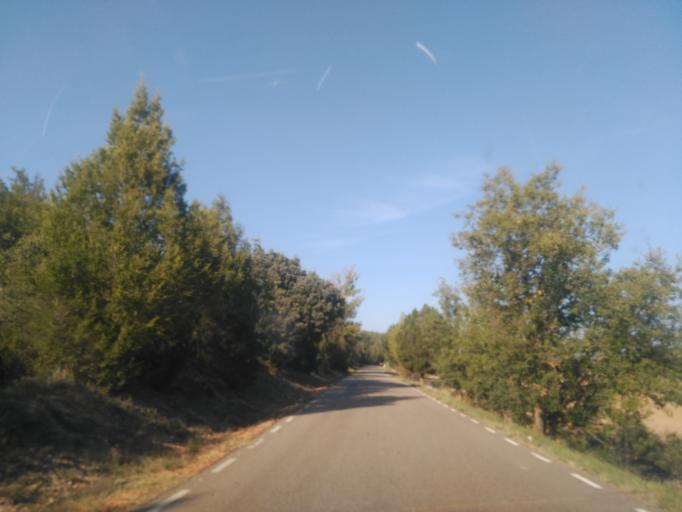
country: ES
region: Castille and Leon
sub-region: Provincia de Burgos
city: Brazacorta
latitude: 41.6951
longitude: -3.4027
